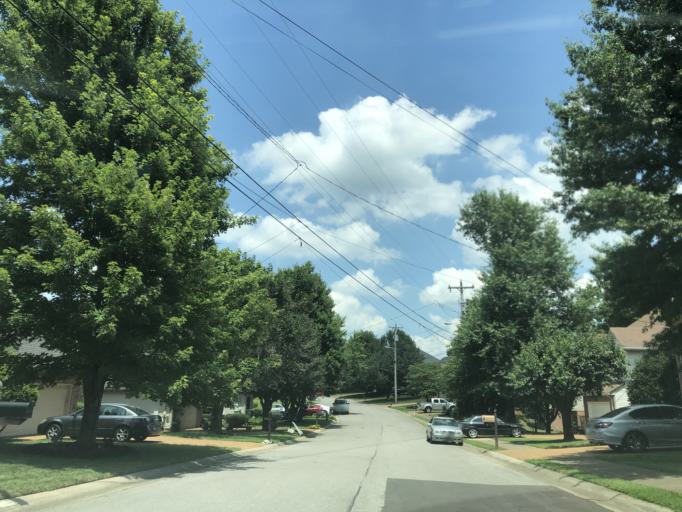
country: US
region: Tennessee
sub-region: Williamson County
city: Brentwood Estates
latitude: 36.0195
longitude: -86.7228
